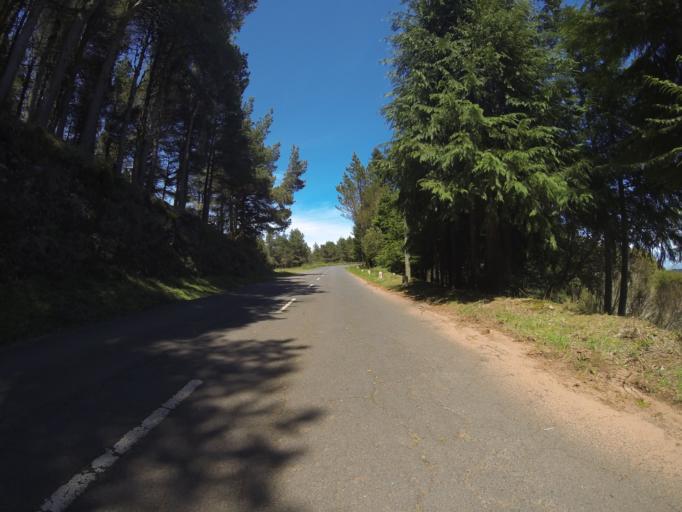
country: PT
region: Madeira
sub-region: Santa Cruz
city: Camacha
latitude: 32.7158
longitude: -16.8805
